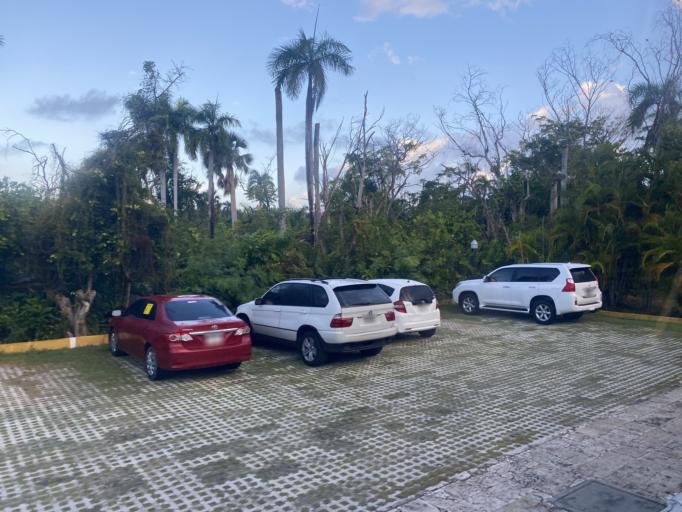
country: DO
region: San Juan
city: Punta Cana
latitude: 18.7308
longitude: -68.4692
